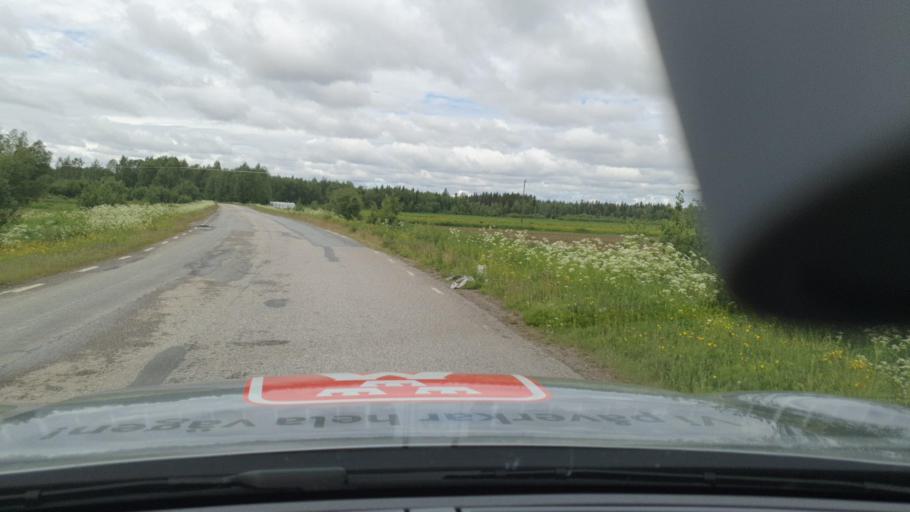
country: SE
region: Norrbotten
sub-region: Lulea Kommun
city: Ranea
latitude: 65.7775
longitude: 22.2238
